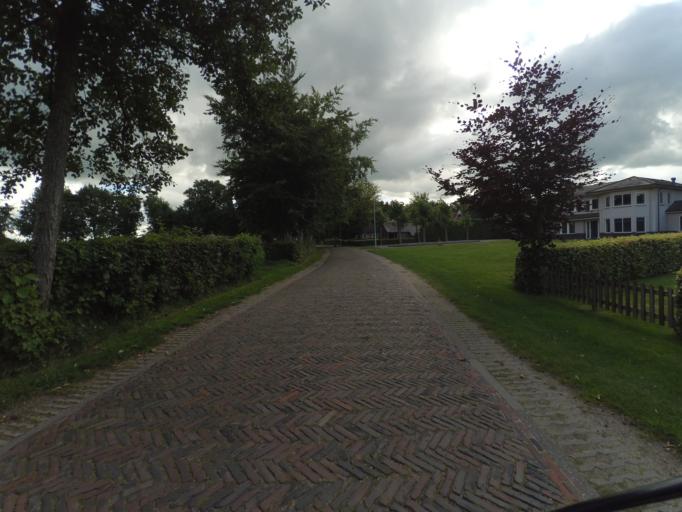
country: NL
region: Friesland
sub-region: Gemeente Tytsjerksteradiel
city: Burgum
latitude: 53.2027
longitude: 5.9932
